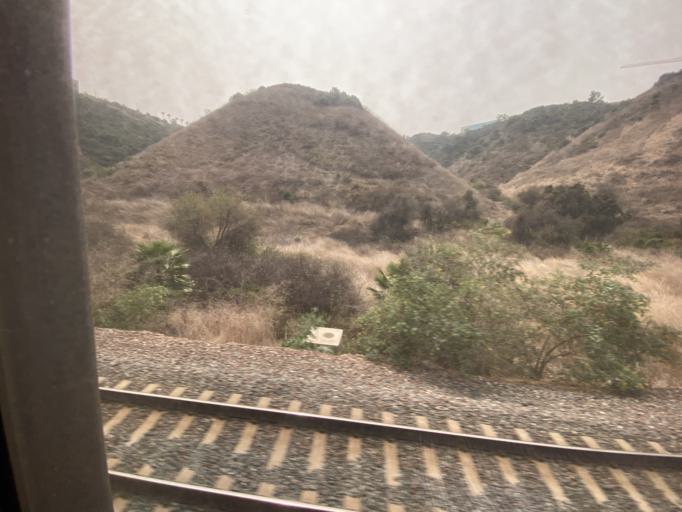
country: US
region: California
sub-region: San Diego County
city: La Jolla
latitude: 32.8870
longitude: -117.2073
